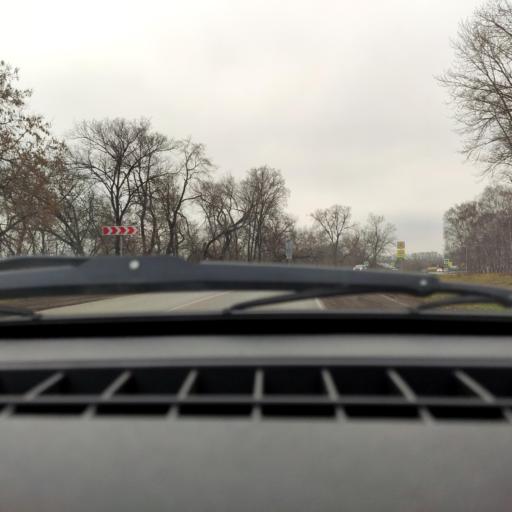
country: RU
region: Bashkortostan
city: Chishmy
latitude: 54.5833
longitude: 55.3806
